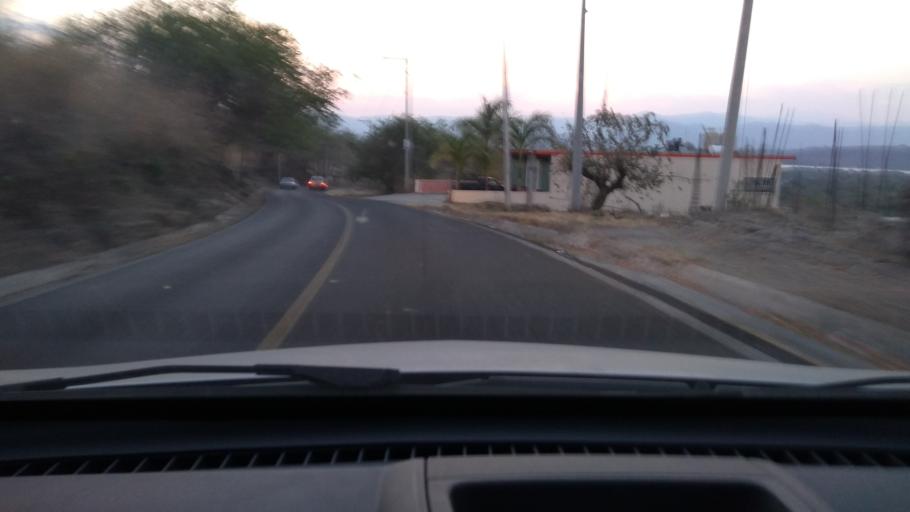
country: MX
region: Morelos
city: Coatetelco
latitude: 18.7223
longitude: -99.3115
